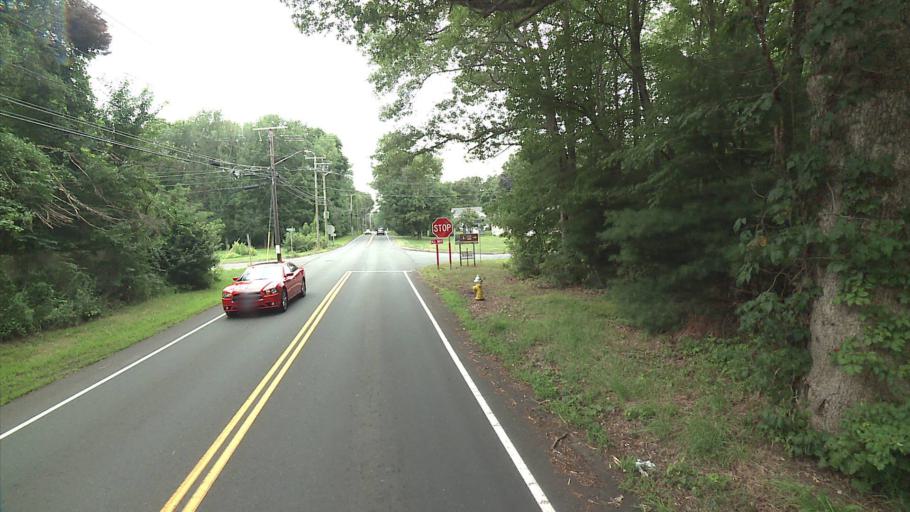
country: US
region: Connecticut
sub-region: Hartford County
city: Broad Brook
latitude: 41.8482
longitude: -72.5245
